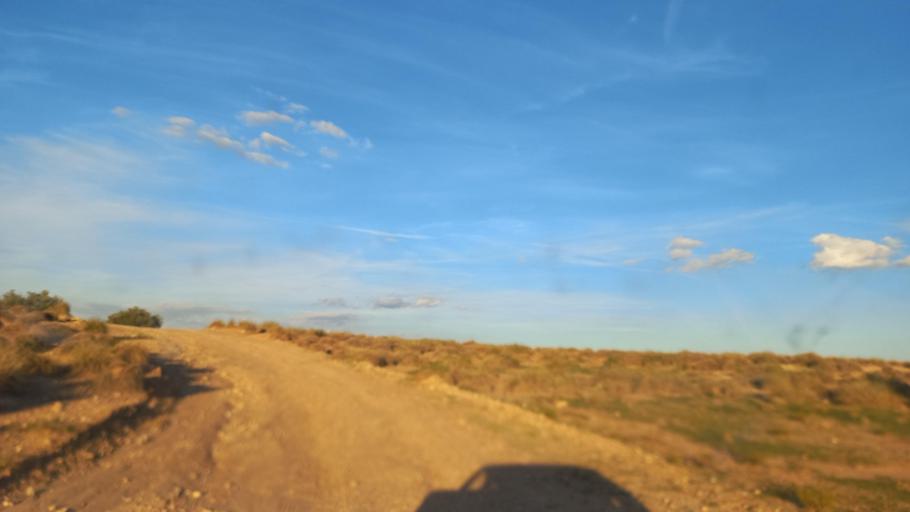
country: TN
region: Al Qasrayn
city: Sbiba
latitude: 35.3486
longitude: 9.0291
